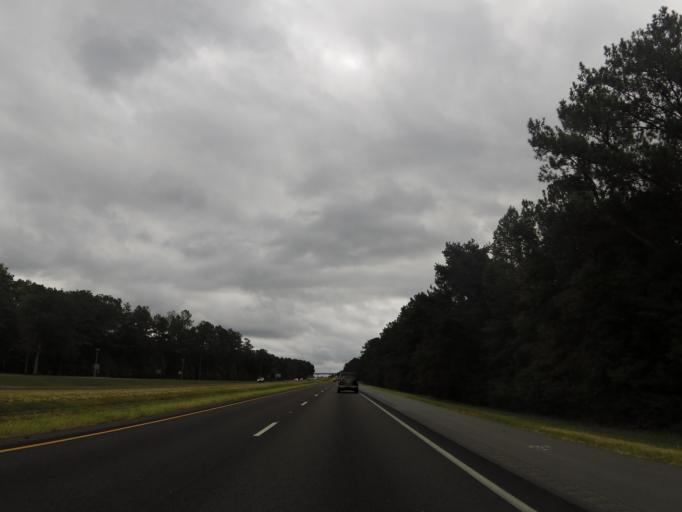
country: US
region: Alabama
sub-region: Conecuh County
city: Evergreen
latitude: 31.3725
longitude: -87.0497
